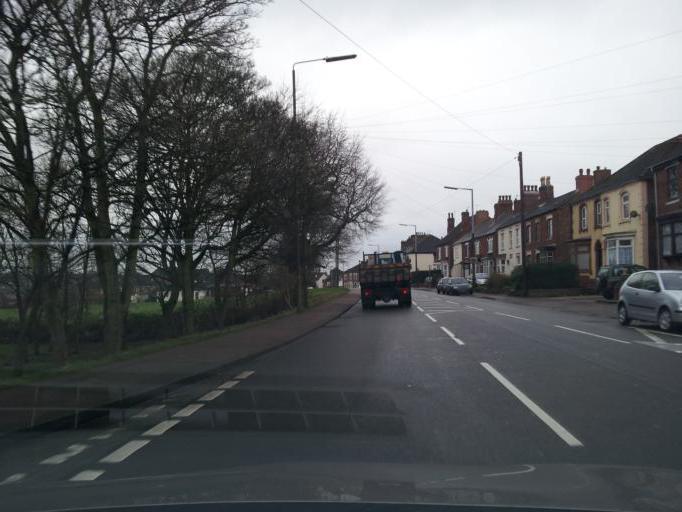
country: GB
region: England
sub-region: Derbyshire
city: Swadlincote
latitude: 52.7726
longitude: -1.5377
